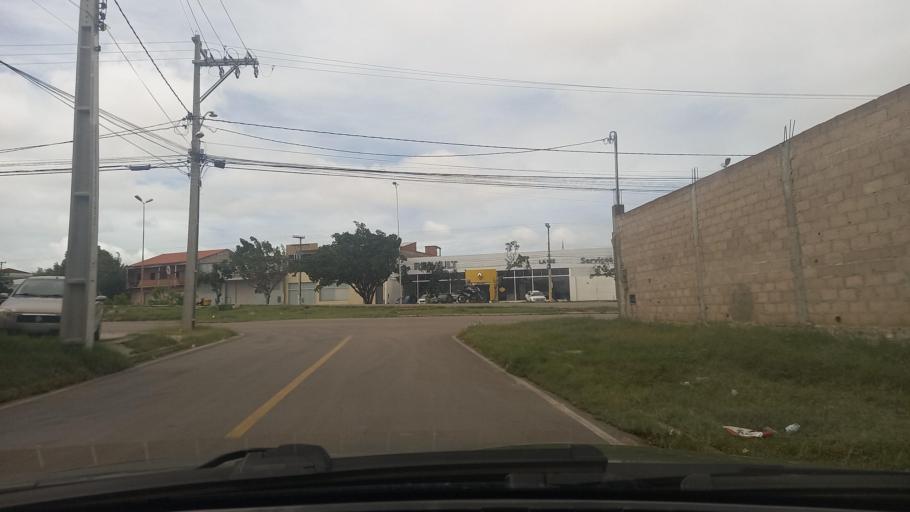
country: BR
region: Bahia
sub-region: Paulo Afonso
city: Paulo Afonso
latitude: -9.4037
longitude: -38.2387
